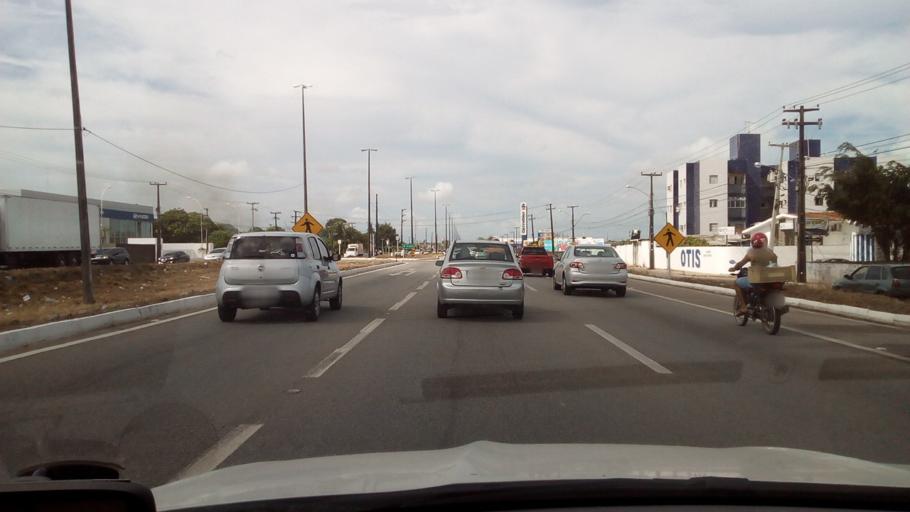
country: BR
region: Paraiba
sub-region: Joao Pessoa
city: Joao Pessoa
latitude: -7.0891
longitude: -34.8484
